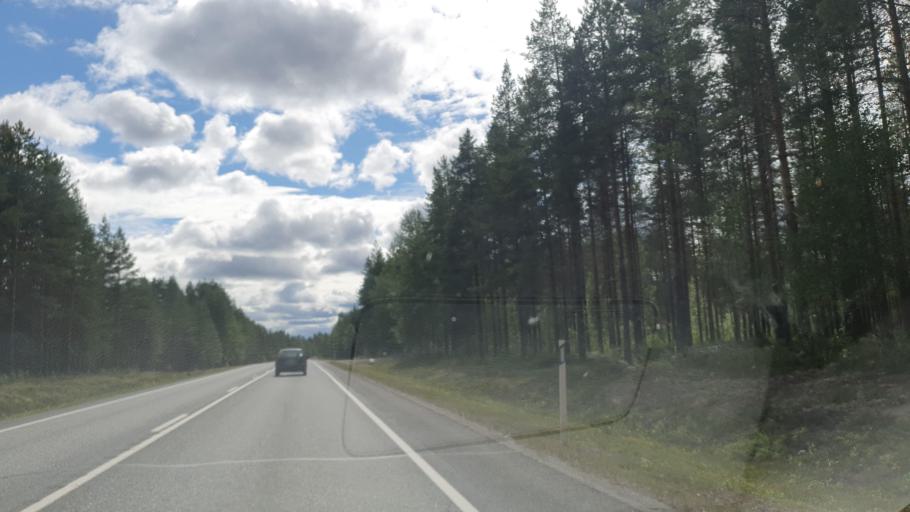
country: FI
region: Kainuu
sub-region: Kajaani
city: Kajaani
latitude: 64.1419
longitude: 27.4982
